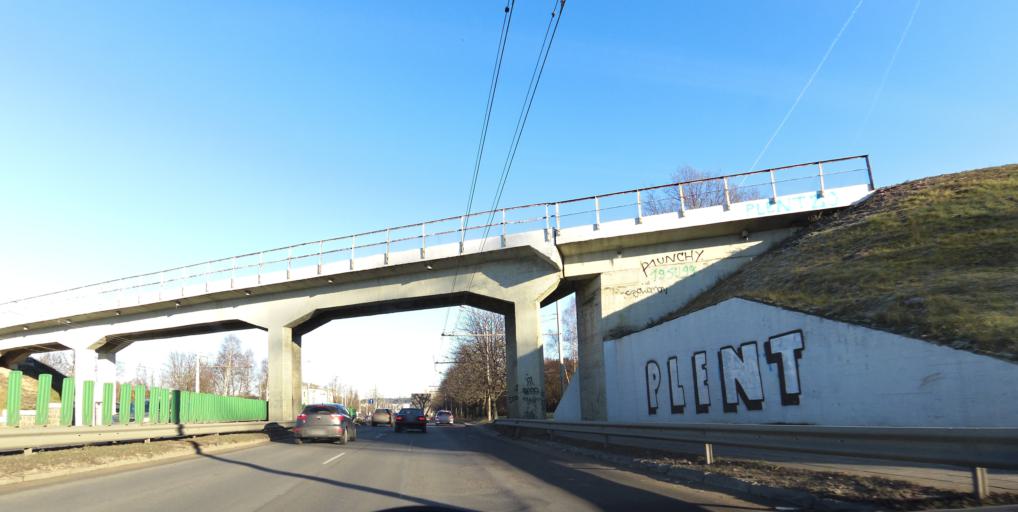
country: LT
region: Vilnius County
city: Lazdynai
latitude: 54.6451
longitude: 25.2081
